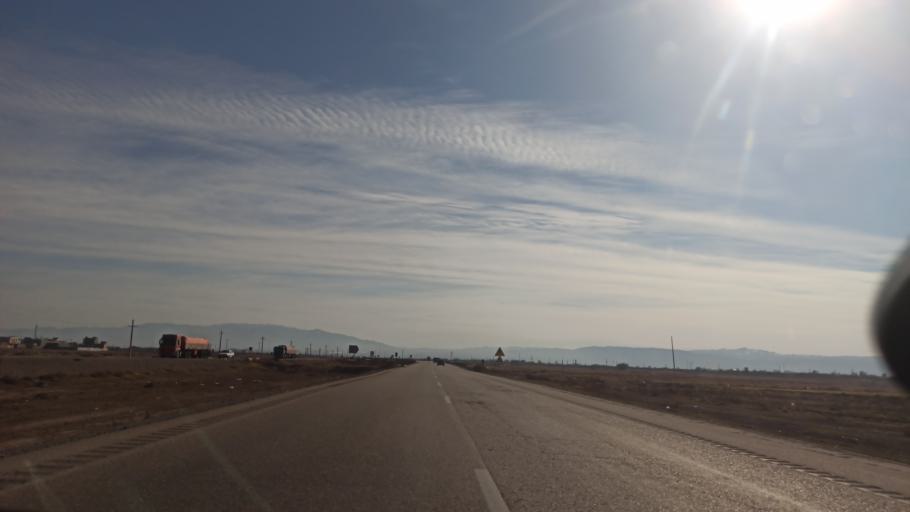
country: IR
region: Qazvin
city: Bu'in Zahra
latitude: 35.7939
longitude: 50.0779
